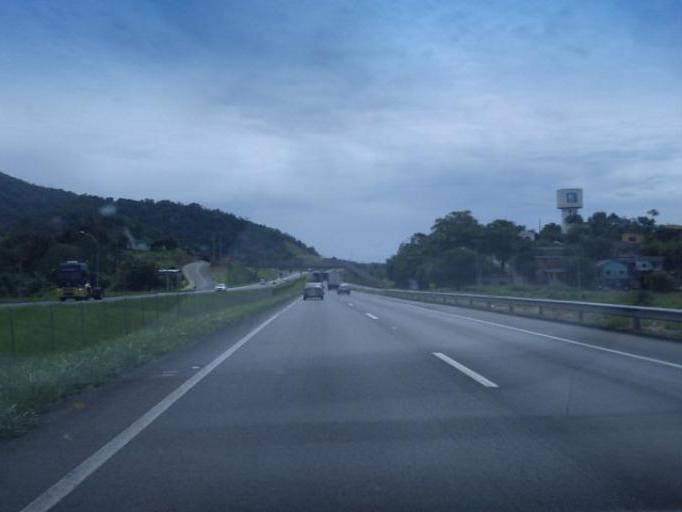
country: BR
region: Sao Paulo
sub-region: Miracatu
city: Miracatu
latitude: -24.2889
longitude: -47.4614
